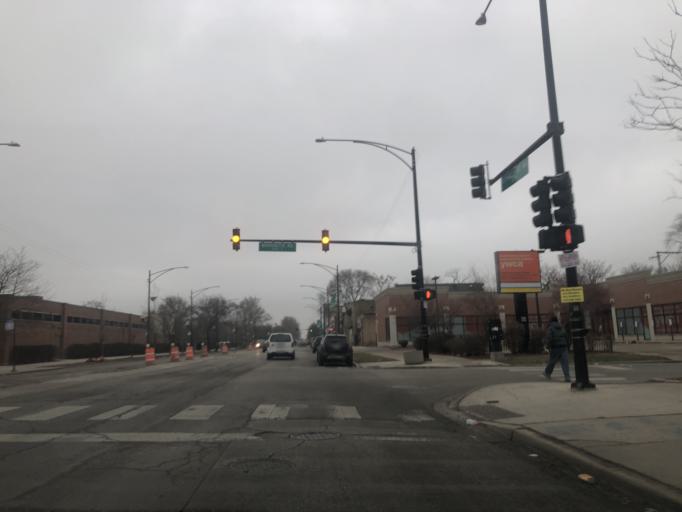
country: US
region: Illinois
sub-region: Cook County
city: Chicago
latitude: 41.7752
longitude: -87.6058
